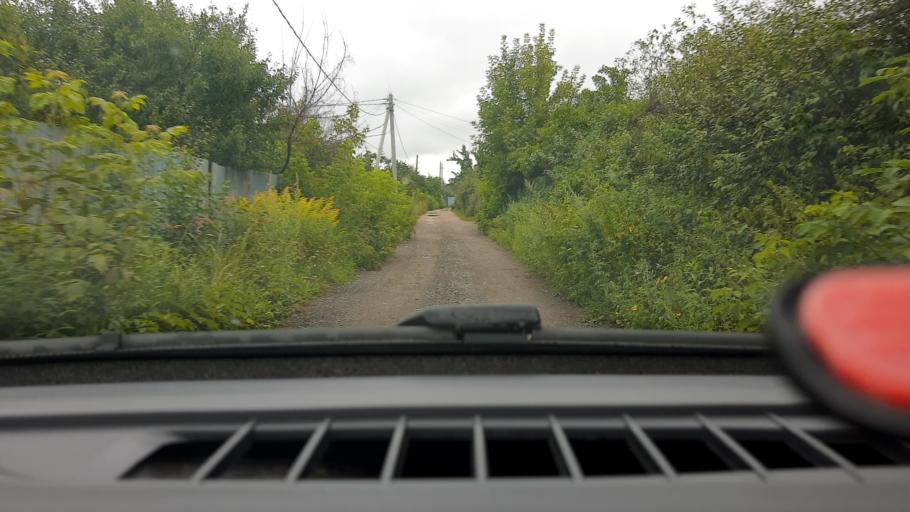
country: RU
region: Nizjnij Novgorod
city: Gorbatovka
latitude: 56.3191
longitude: 43.8370
